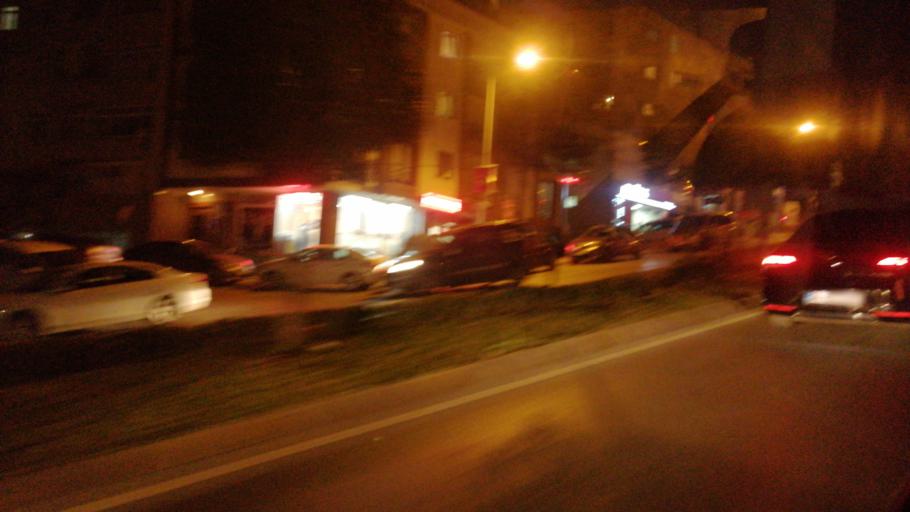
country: TR
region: Istanbul
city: Umraniye
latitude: 41.0081
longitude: 29.1271
